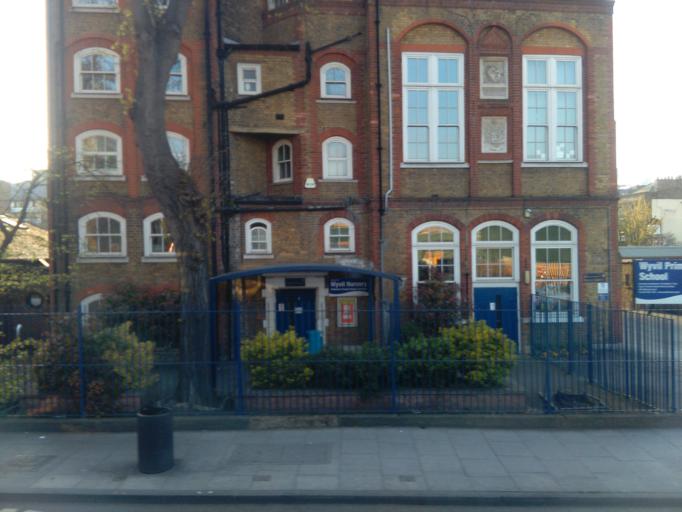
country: GB
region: England
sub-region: Greater London
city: Lambeth
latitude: 51.4815
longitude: -0.1245
